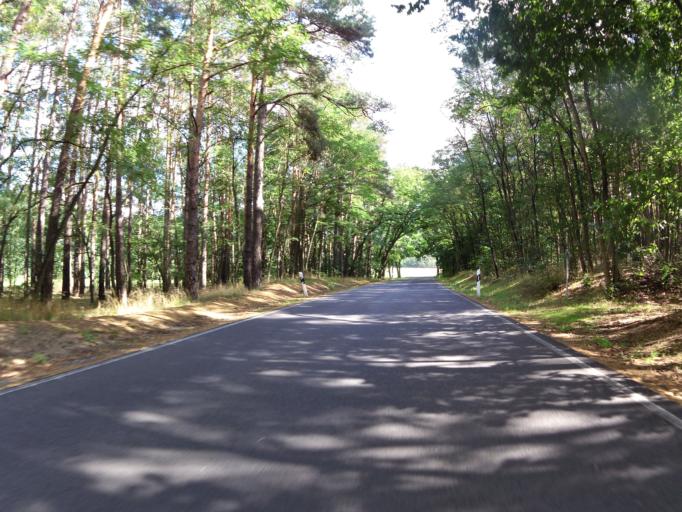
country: DE
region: Brandenburg
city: Munchehofe
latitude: 52.1991
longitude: 13.8583
